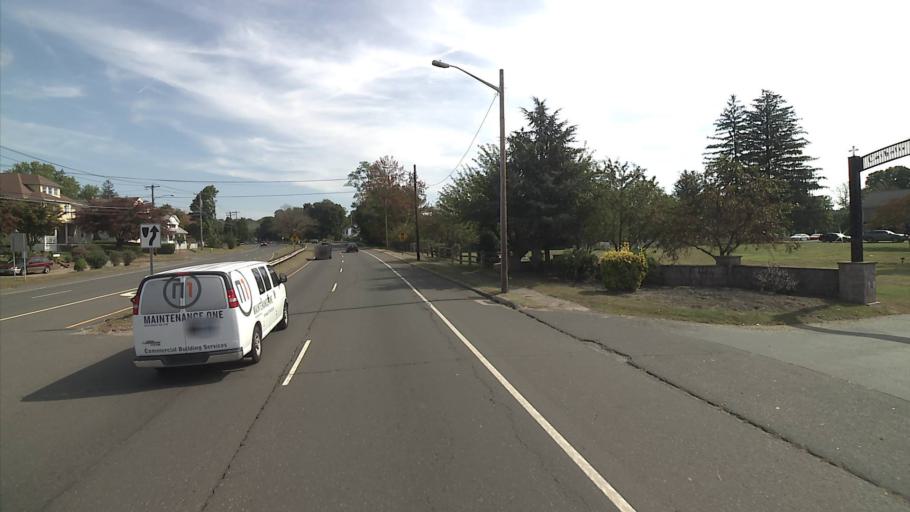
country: US
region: Connecticut
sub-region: New Haven County
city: Derby
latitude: 41.3075
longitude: -73.0684
